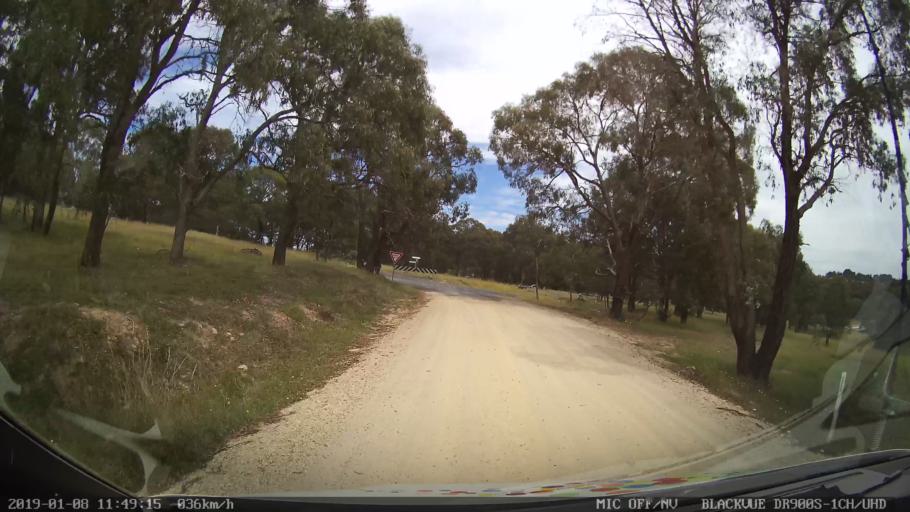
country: AU
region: New South Wales
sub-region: Armidale Dumaresq
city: Armidale
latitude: -30.3744
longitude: 151.5588
